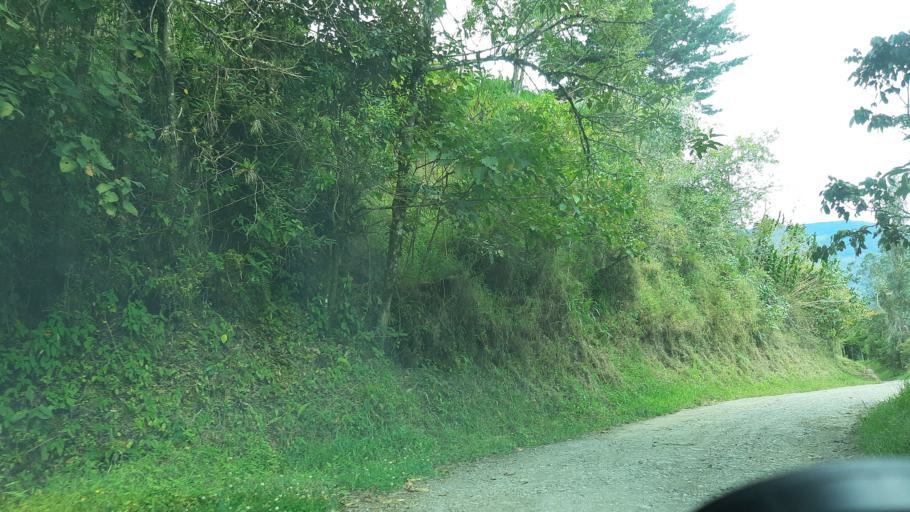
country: CO
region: Boyaca
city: Garagoa
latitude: 5.0481
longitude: -73.3503
